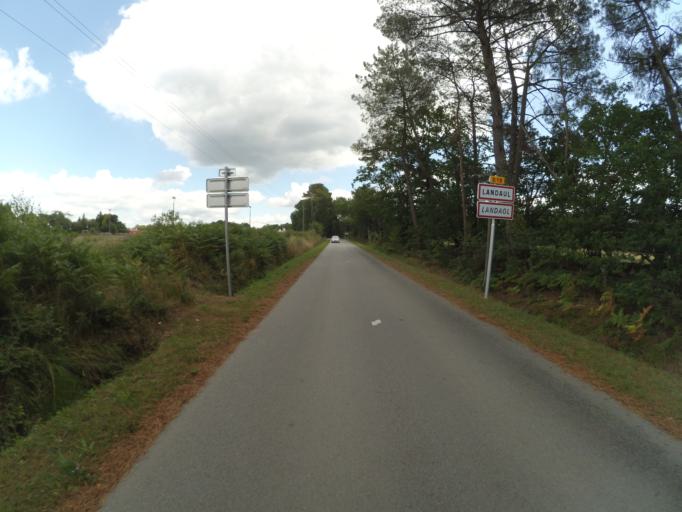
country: FR
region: Brittany
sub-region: Departement du Morbihan
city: Landaul
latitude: 47.7469
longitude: -3.0865
